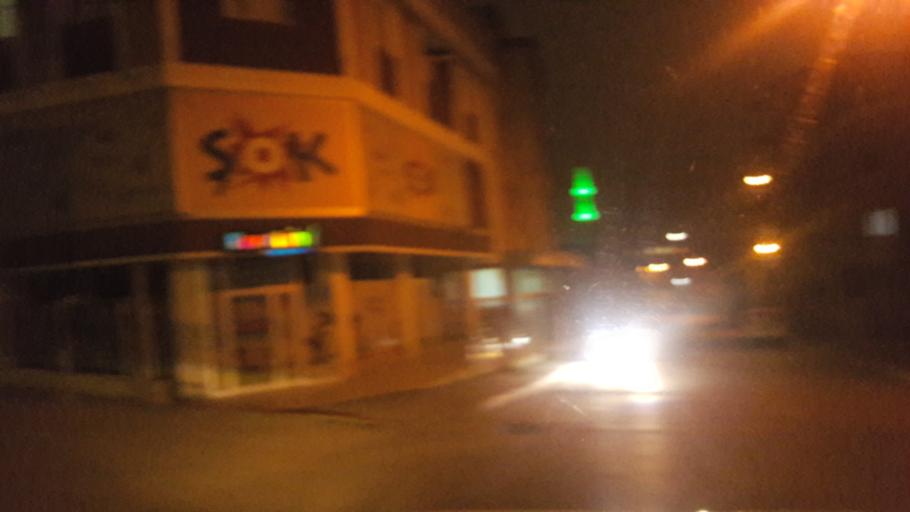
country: TR
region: Kocaeli
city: Tavsancil
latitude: 40.7843
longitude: 29.5417
